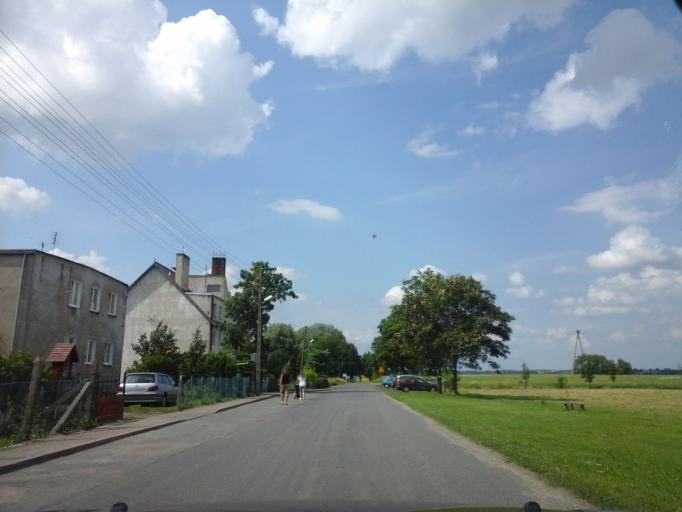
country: PL
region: West Pomeranian Voivodeship
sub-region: Powiat choszczenski
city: Pelczyce
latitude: 53.0758
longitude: 15.3748
